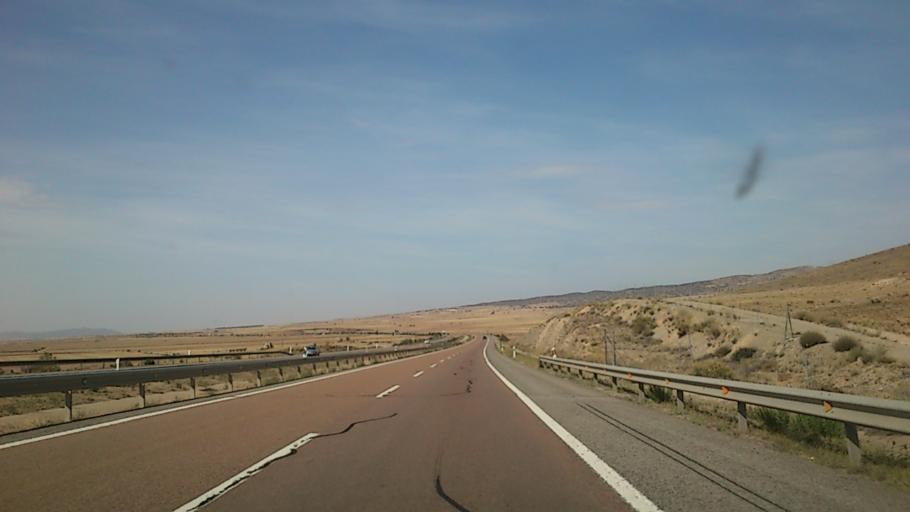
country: ES
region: Aragon
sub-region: Provincia de Teruel
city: Singra
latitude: 40.6615
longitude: -1.3171
